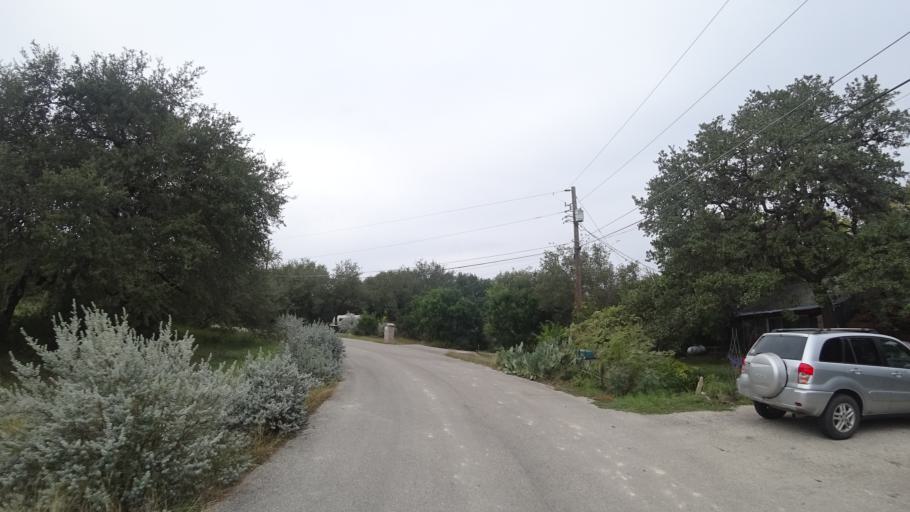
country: US
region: Texas
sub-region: Travis County
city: Hudson Bend
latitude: 30.3706
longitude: -97.9205
